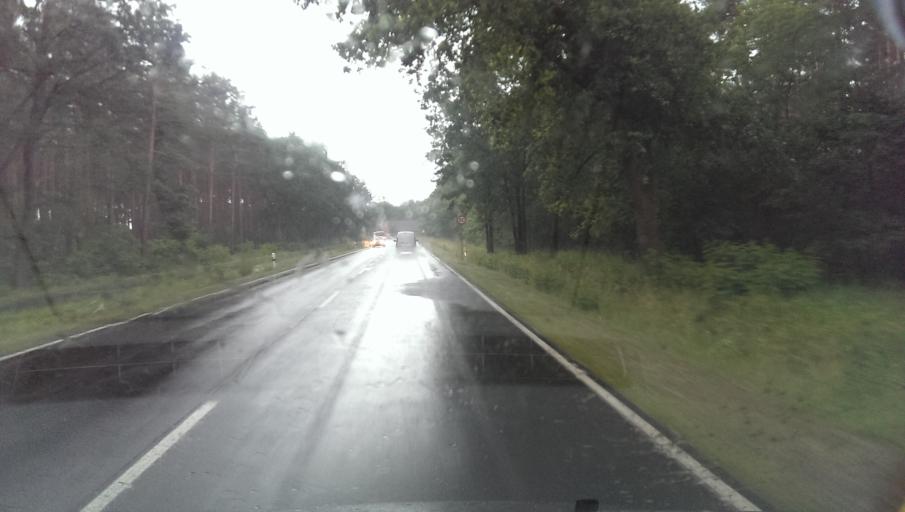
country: DE
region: Brandenburg
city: Premnitz
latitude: 52.5182
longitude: 12.3996
